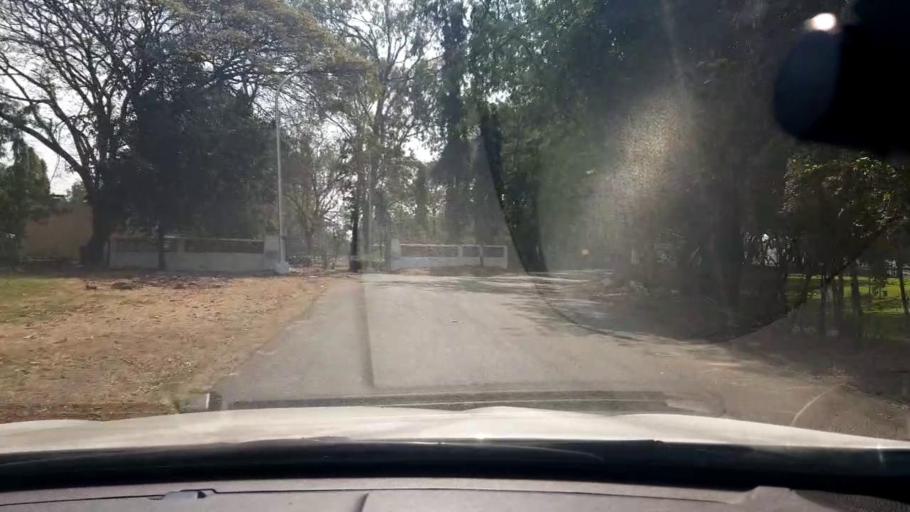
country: IN
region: Maharashtra
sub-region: Pune Division
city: Shivaji Nagar
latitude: 18.5461
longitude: 73.8593
